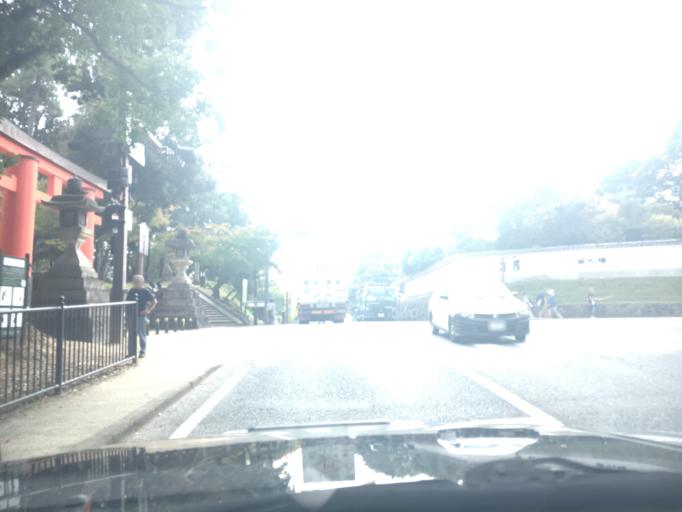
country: JP
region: Nara
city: Nara-shi
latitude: 34.6823
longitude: 135.8348
